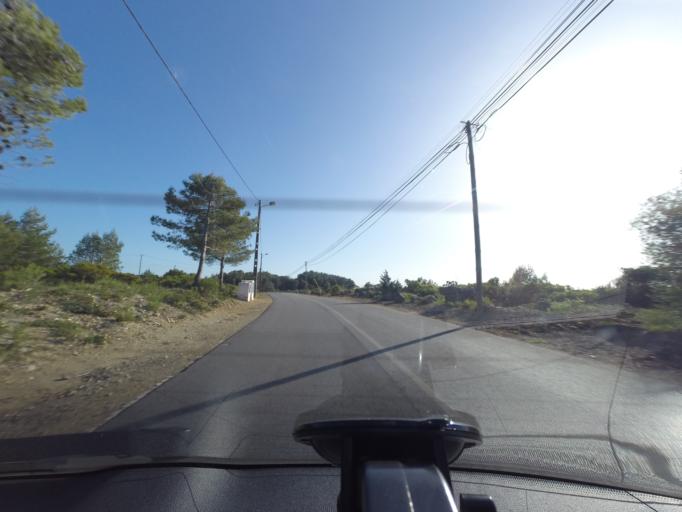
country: PT
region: Lisbon
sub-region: Cascais
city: Alcabideche
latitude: 38.7387
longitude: -9.4382
